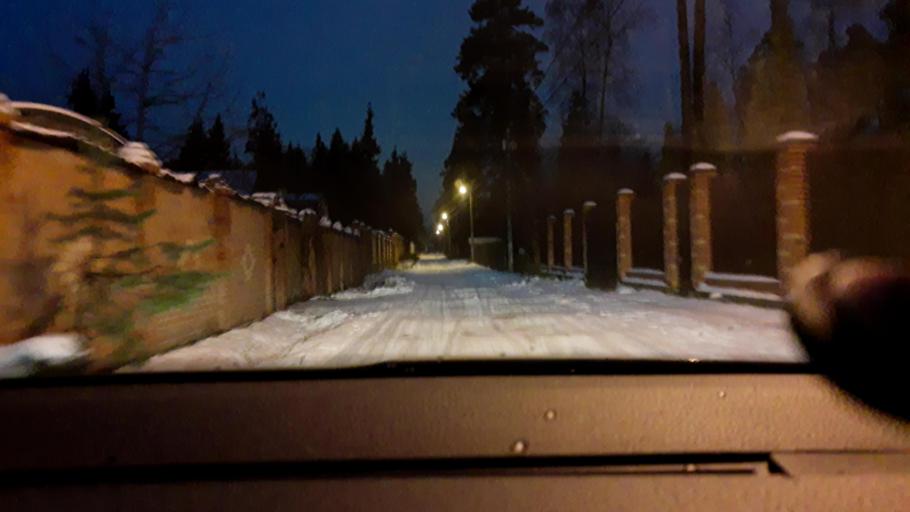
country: RU
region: Moskovskaya
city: Saltykovka
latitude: 55.7761
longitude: 37.9634
